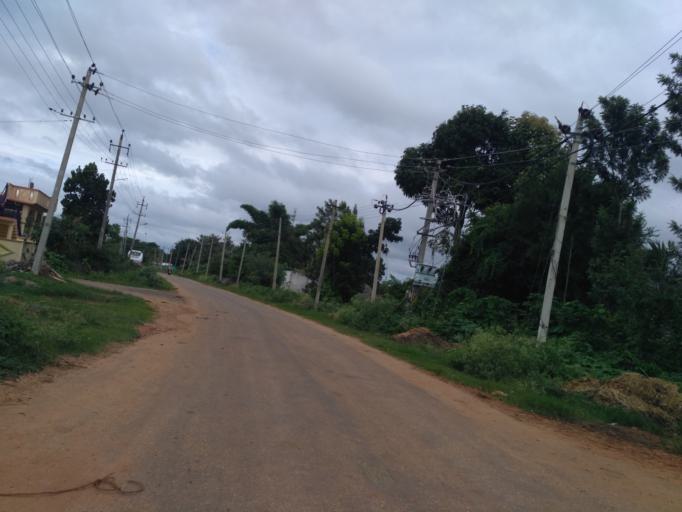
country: IN
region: Karnataka
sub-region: Hassan
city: Gorur
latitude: 12.8239
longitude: 76.0826
